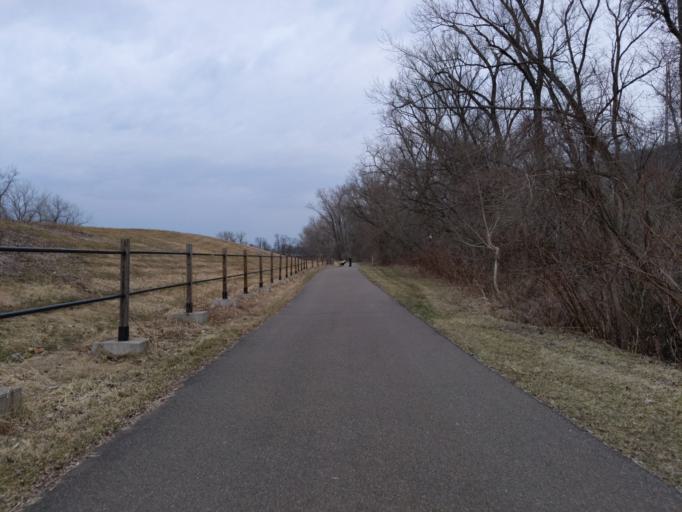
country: US
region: New York
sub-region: Chemung County
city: Elmira
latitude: 42.0911
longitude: -76.7845
